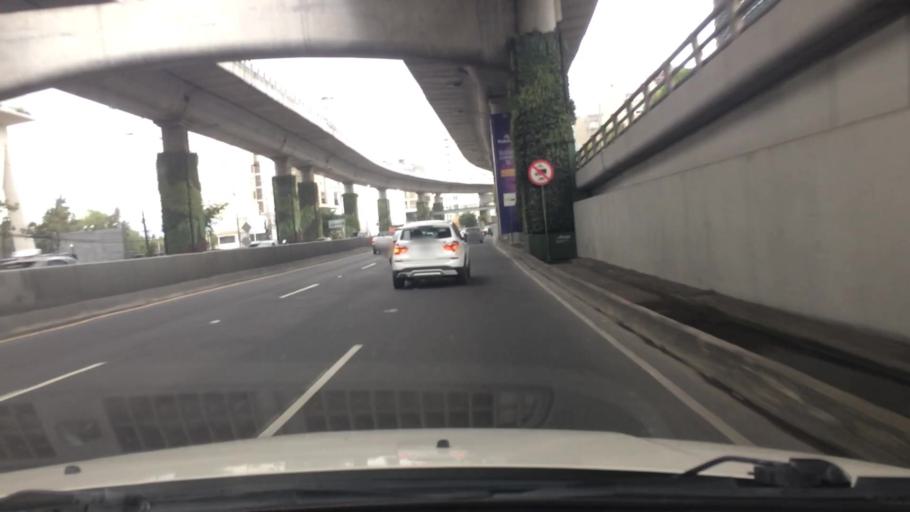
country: MX
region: Mexico City
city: Alvaro Obregon
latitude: 19.3590
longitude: -99.1941
